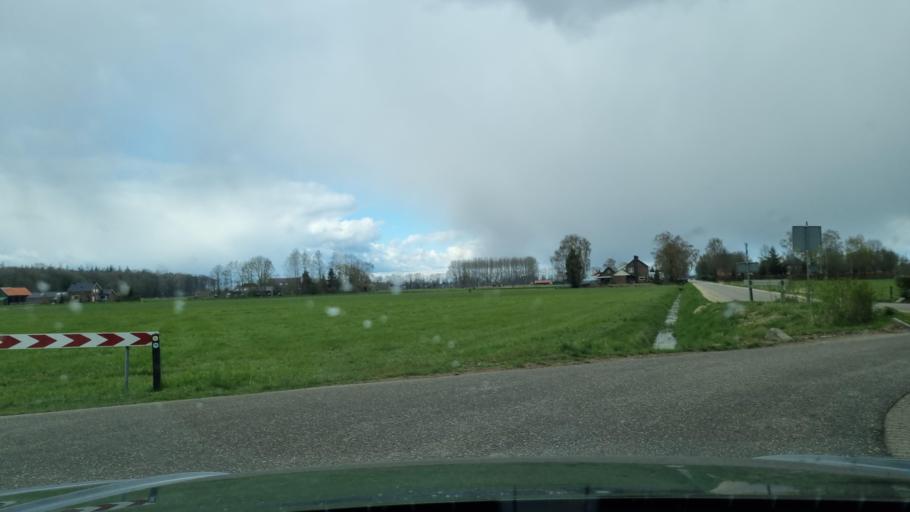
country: NL
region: Gelderland
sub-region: Gemeente Montferland
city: s-Heerenberg
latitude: 51.9019
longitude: 6.1761
